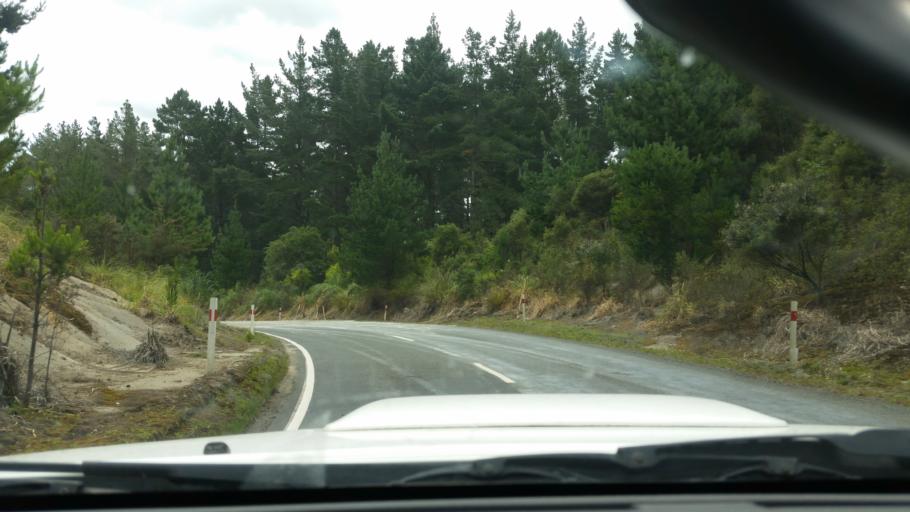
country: NZ
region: Northland
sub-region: Kaipara District
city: Dargaville
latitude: -35.7288
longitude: 173.8624
